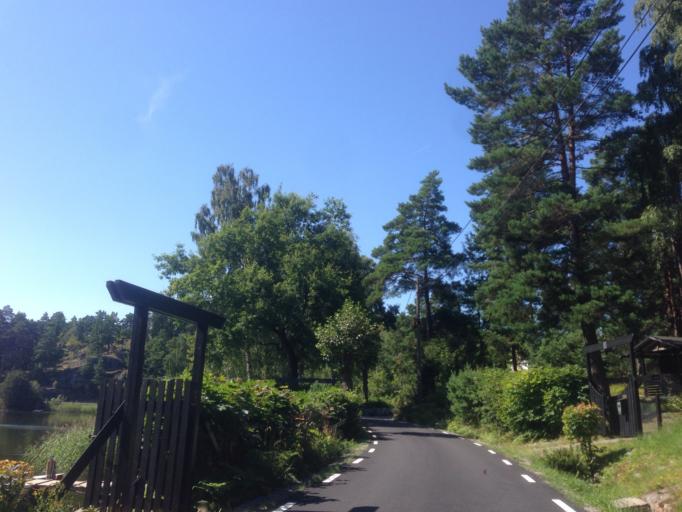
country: SE
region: Stockholm
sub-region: Vaxholms Kommun
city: Vaxholm
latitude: 59.3880
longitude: 18.3712
